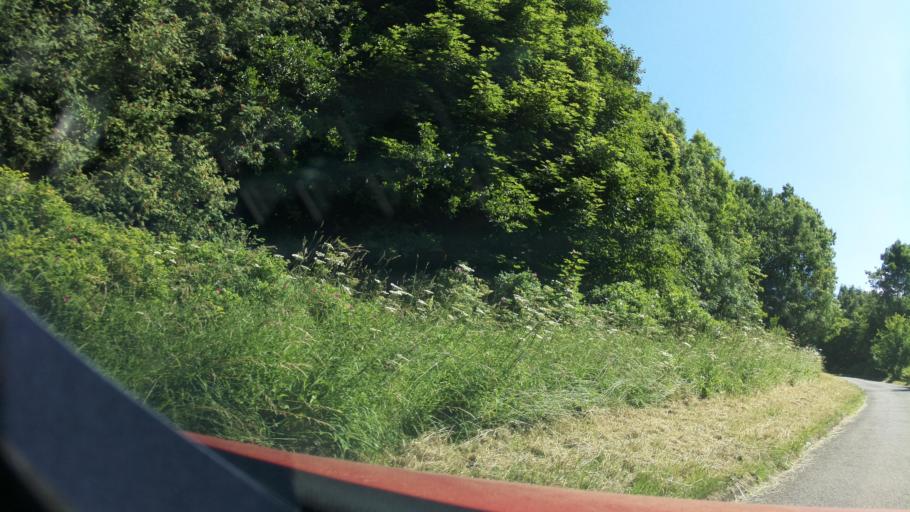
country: GB
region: England
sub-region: Derbyshire
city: Buxton
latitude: 53.2874
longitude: -1.8623
